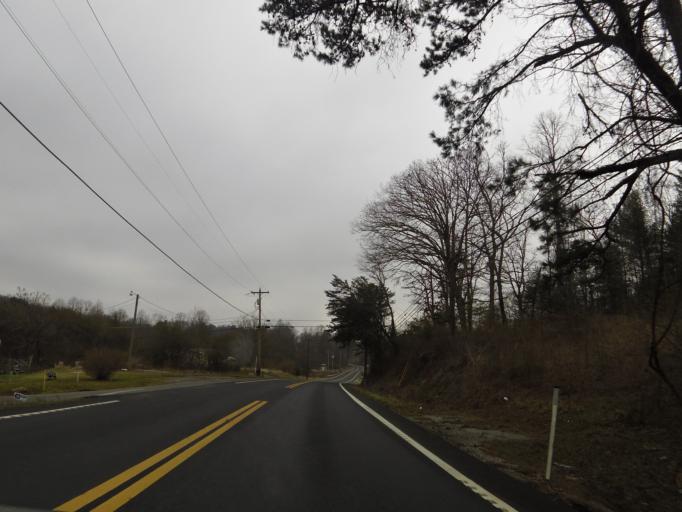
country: US
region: Tennessee
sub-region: Morgan County
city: Wartburg
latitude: 36.0838
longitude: -84.5527
